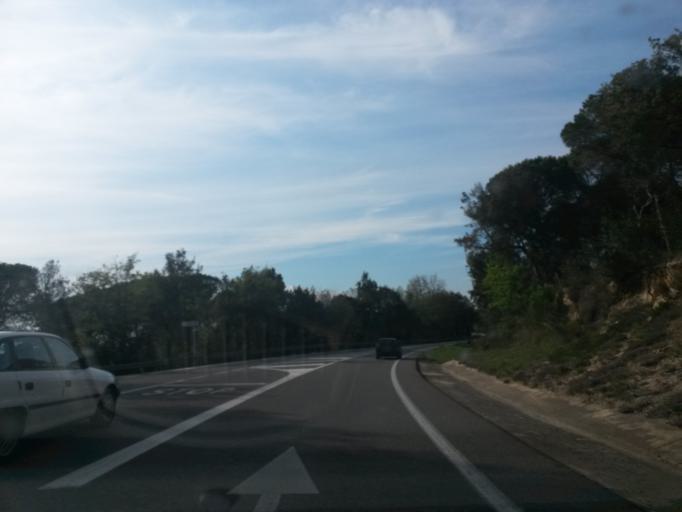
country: ES
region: Catalonia
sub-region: Provincia de Girona
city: Caldes de Malavella
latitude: 41.8449
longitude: 2.7805
